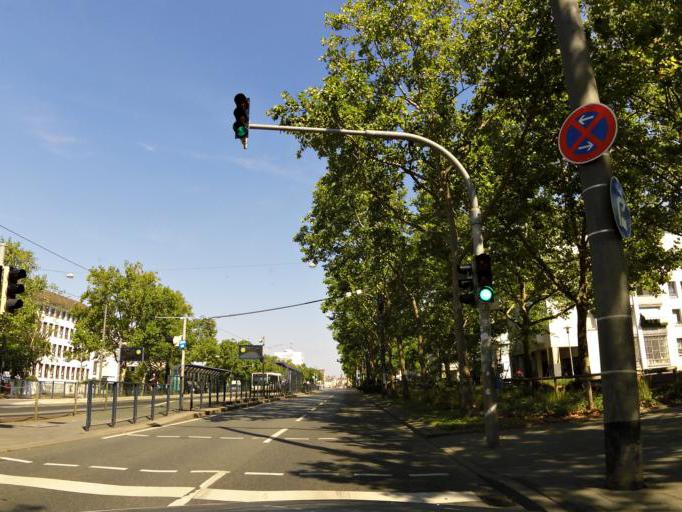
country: DE
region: Hesse
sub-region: Regierungsbezirk Darmstadt
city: Darmstadt
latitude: 49.8705
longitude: 8.6352
